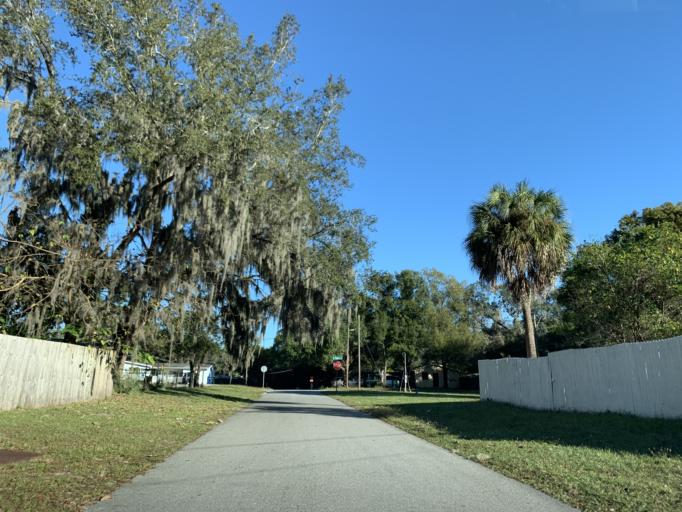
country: US
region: Florida
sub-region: Hillsborough County
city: University
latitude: 28.0364
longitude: -82.4326
